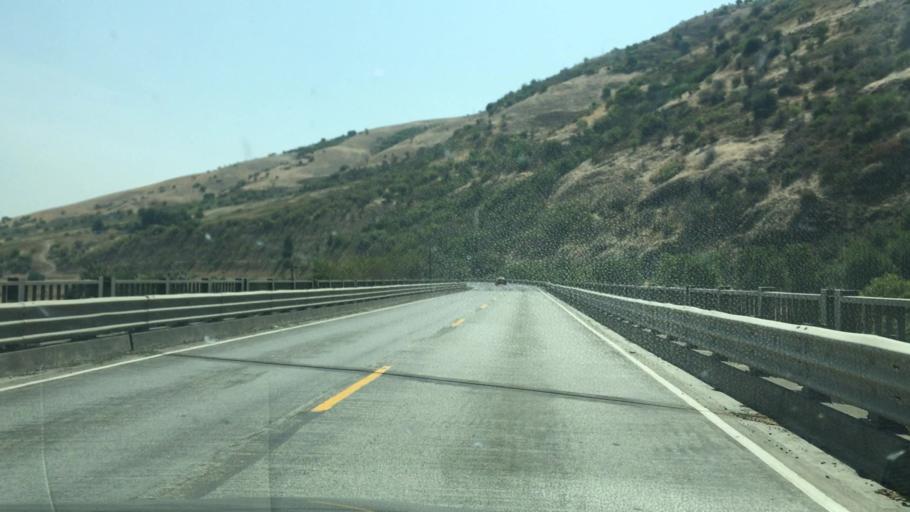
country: US
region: Idaho
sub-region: Nez Perce County
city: Lapwai
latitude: 46.4418
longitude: -116.8455
